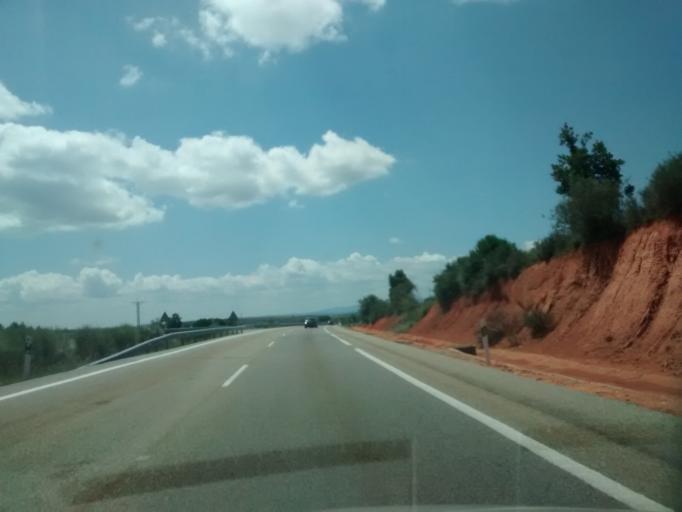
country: ES
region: Castille and Leon
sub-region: Provincia de Leon
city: Brazuelo
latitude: 42.5064
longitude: -6.1178
